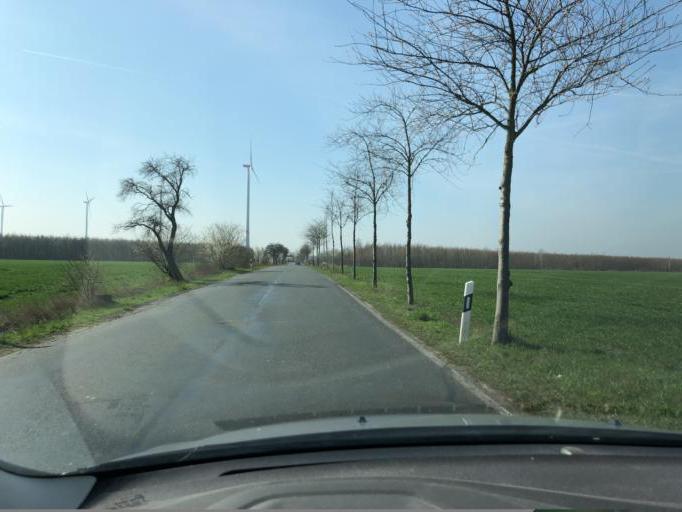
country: DE
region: Saxony
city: Krostitz
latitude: 51.4174
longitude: 12.4414
